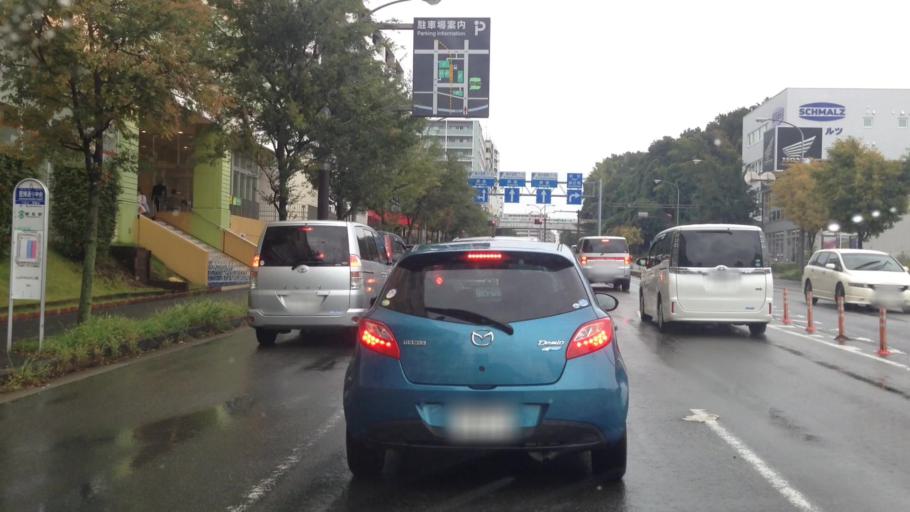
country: JP
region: Tokyo
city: Chofugaoka
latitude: 35.5483
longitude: 139.5781
